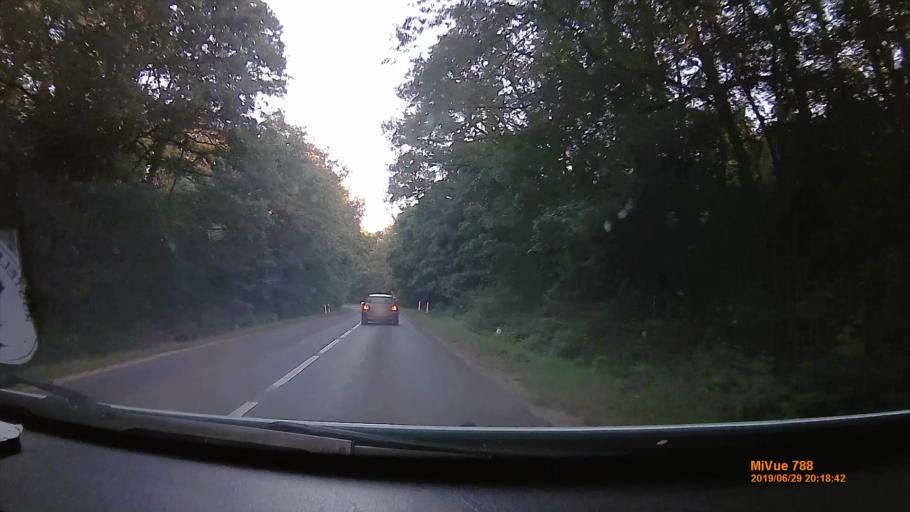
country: HU
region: Pest
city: Paty
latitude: 47.5038
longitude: 18.8590
